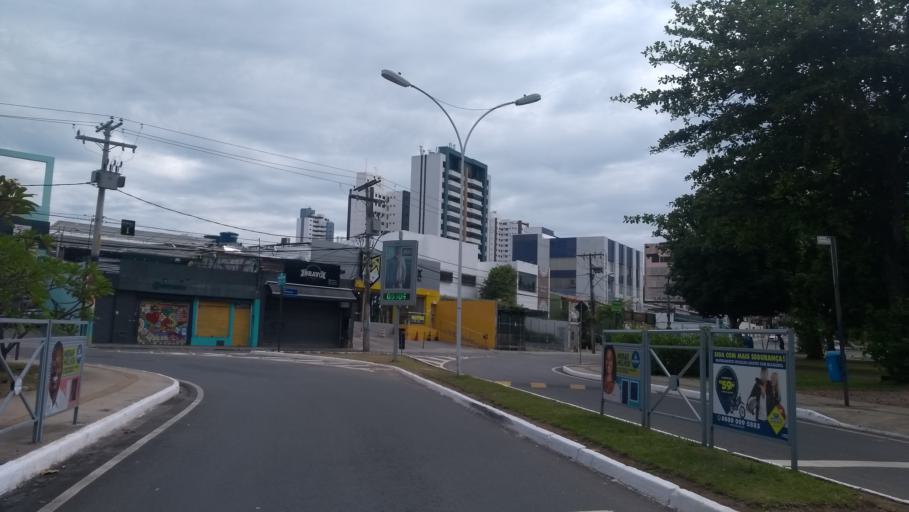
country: BR
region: Bahia
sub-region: Salvador
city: Salvador
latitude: -12.9944
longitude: -38.4600
